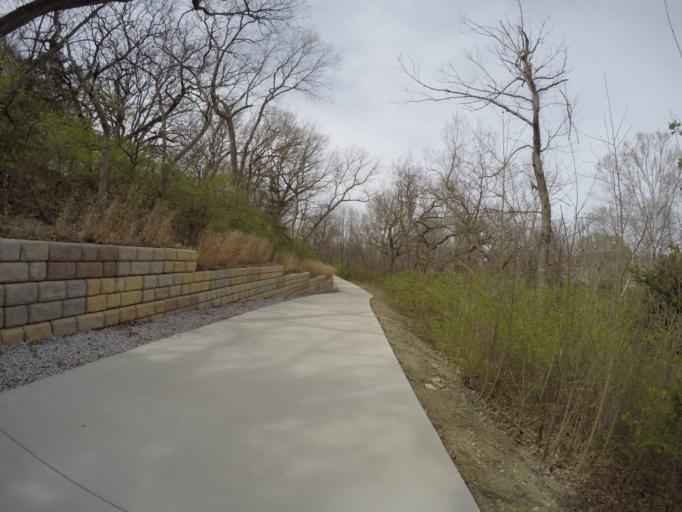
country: US
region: Kansas
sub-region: Johnson County
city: Leawood
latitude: 38.9084
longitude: -94.6327
